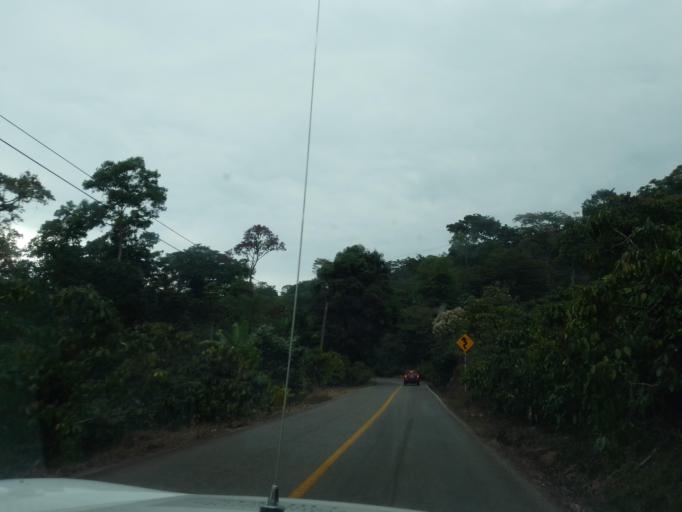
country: MX
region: Chiapas
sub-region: Union Juarez
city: Santo Domingo
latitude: 15.0385
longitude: -92.1258
